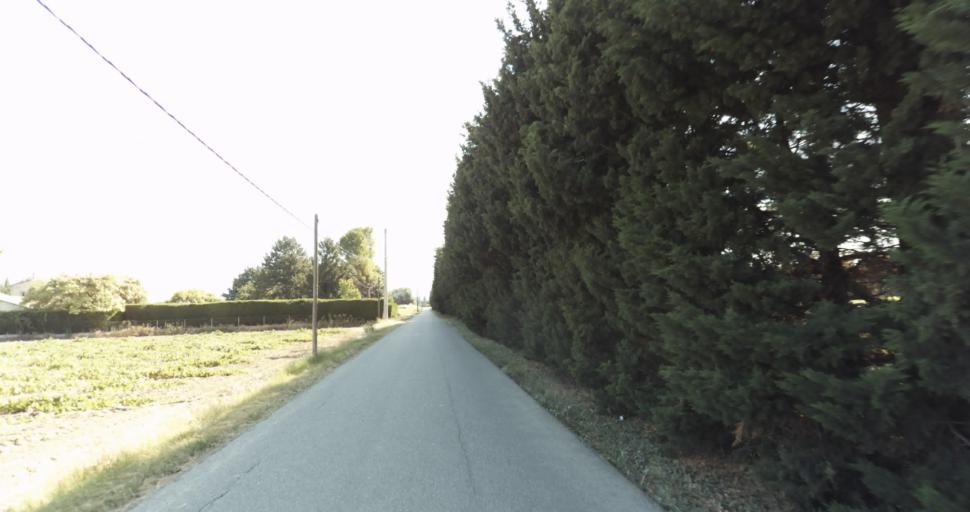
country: FR
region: Provence-Alpes-Cote d'Azur
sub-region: Departement du Vaucluse
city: Althen-des-Paluds
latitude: 44.0082
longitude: 4.9852
